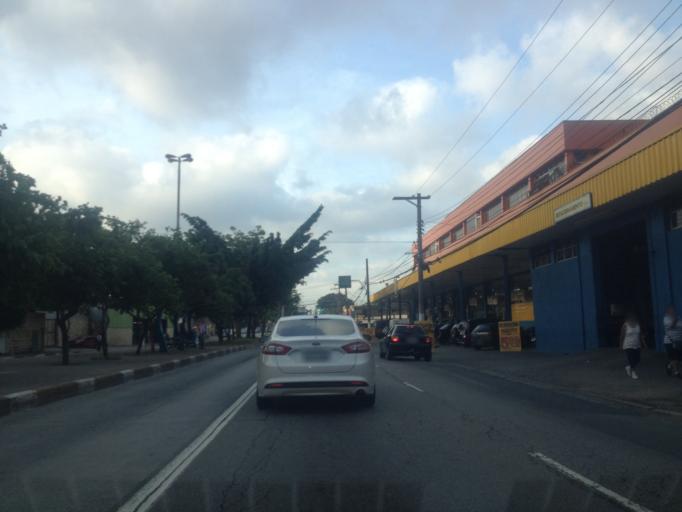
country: BR
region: Sao Paulo
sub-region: Diadema
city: Diadema
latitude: -23.6726
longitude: -46.7121
